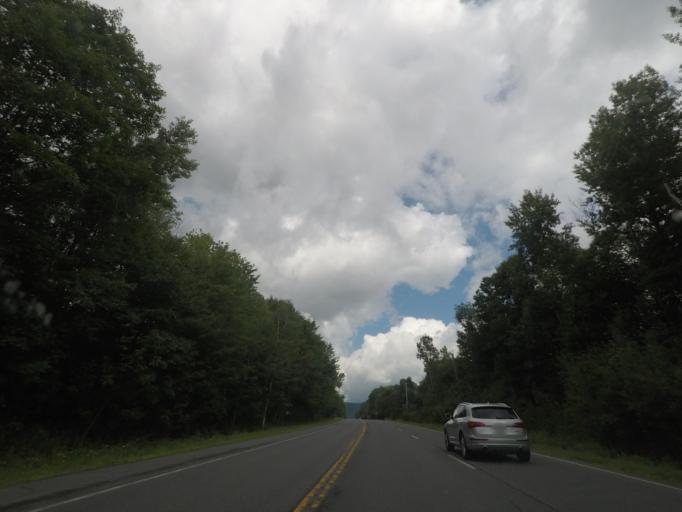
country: US
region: Massachusetts
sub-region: Berkshire County
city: Lanesborough
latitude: 42.6007
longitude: -73.3706
